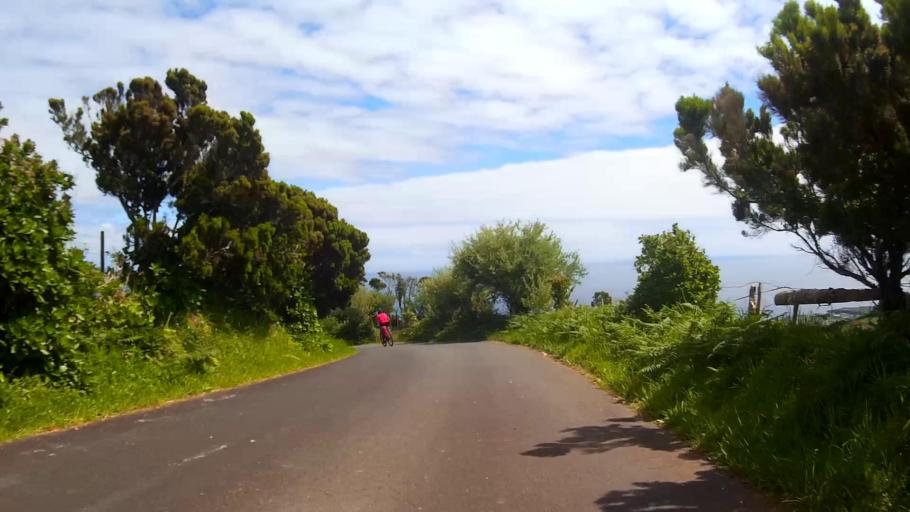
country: PT
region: Azores
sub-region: Horta
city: Horta
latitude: 38.5516
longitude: -28.6720
